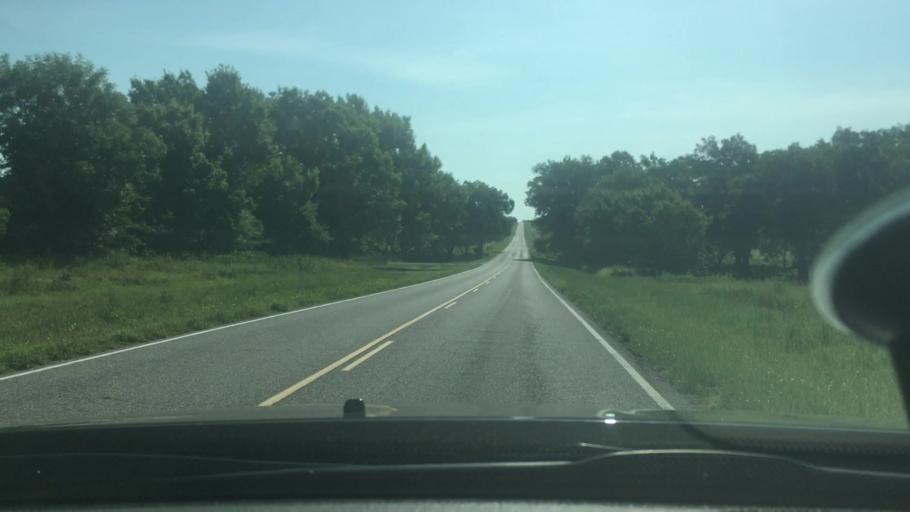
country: US
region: Oklahoma
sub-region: Garvin County
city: Pauls Valley
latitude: 34.6519
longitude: -97.2967
